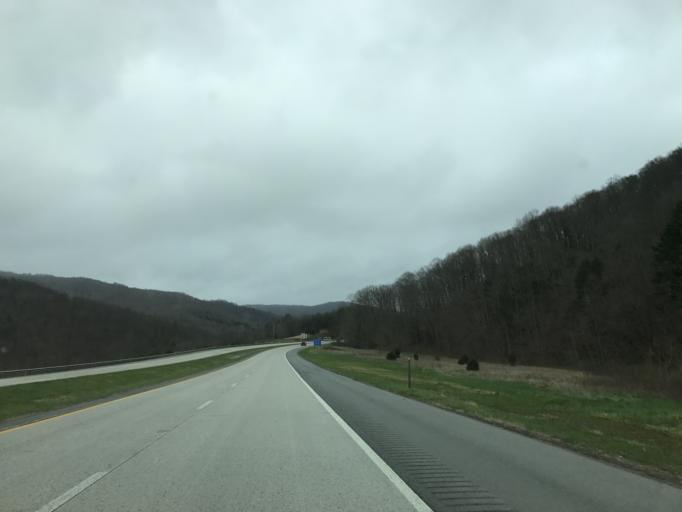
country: US
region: West Virginia
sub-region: Summers County
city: Hinton
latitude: 37.7890
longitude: -80.8758
